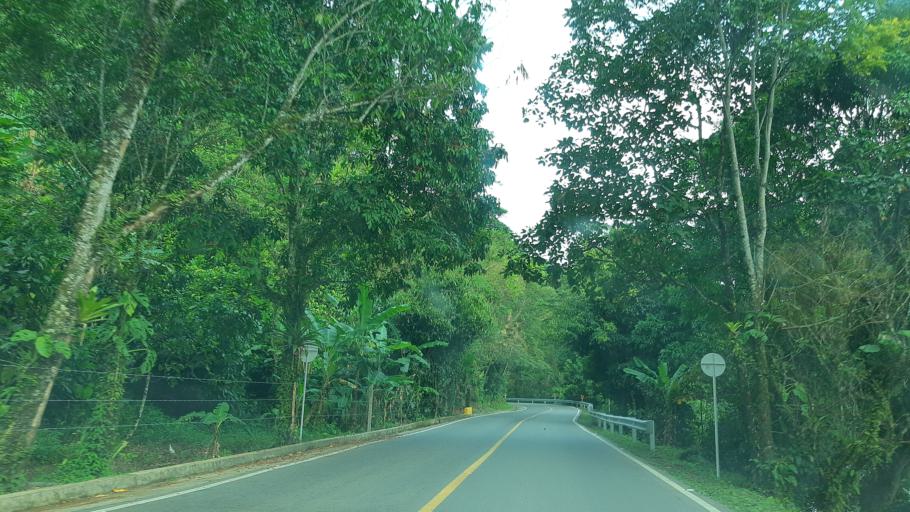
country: CO
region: Boyaca
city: Santa Maria
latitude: 4.8408
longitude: -73.2158
